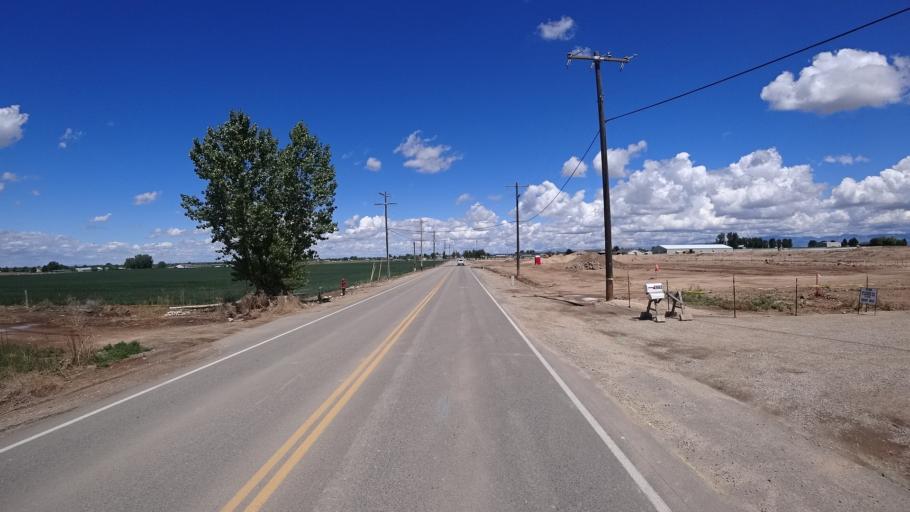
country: US
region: Idaho
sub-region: Ada County
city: Kuna
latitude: 43.5136
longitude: -116.4337
